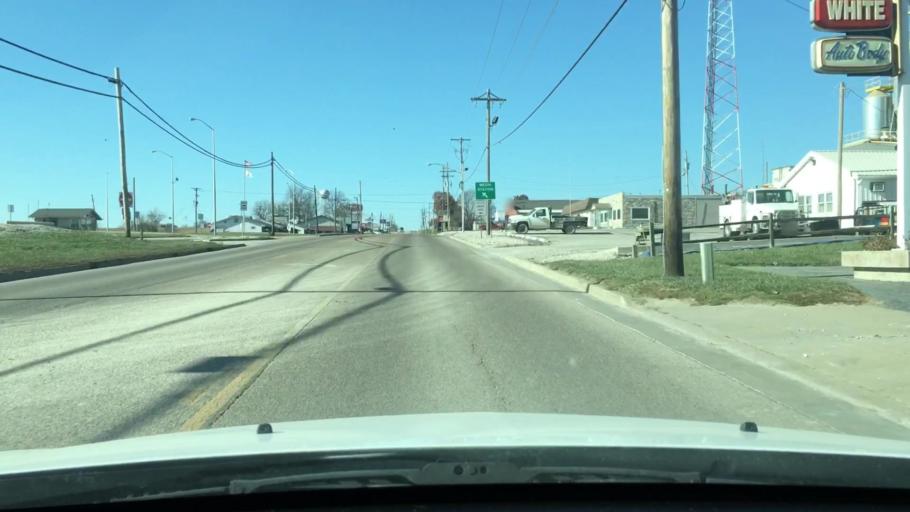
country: US
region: Illinois
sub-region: Pike County
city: Pittsfield
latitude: 39.6046
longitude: -90.8304
